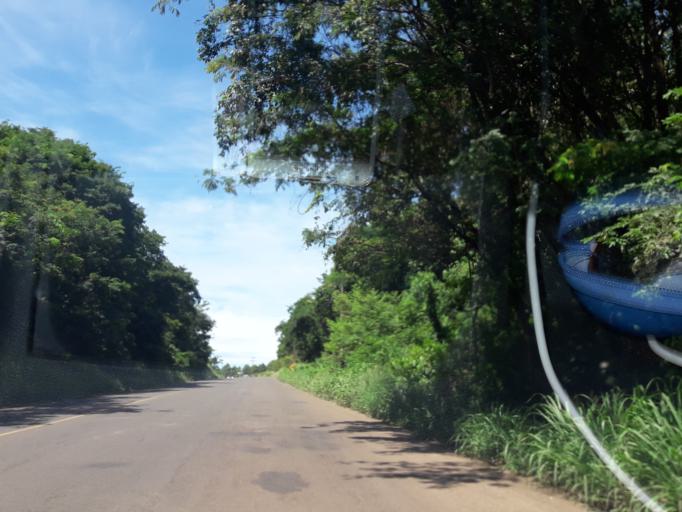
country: AR
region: Misiones
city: Bernardo de Irigoyen
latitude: -26.5815
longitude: -53.5169
